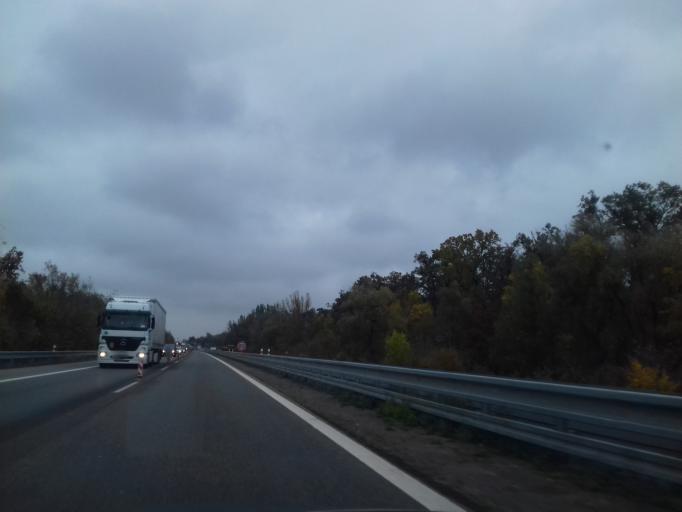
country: CZ
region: South Moravian
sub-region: Okres Breclav
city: Lanzhot
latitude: 48.7116
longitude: 16.9865
